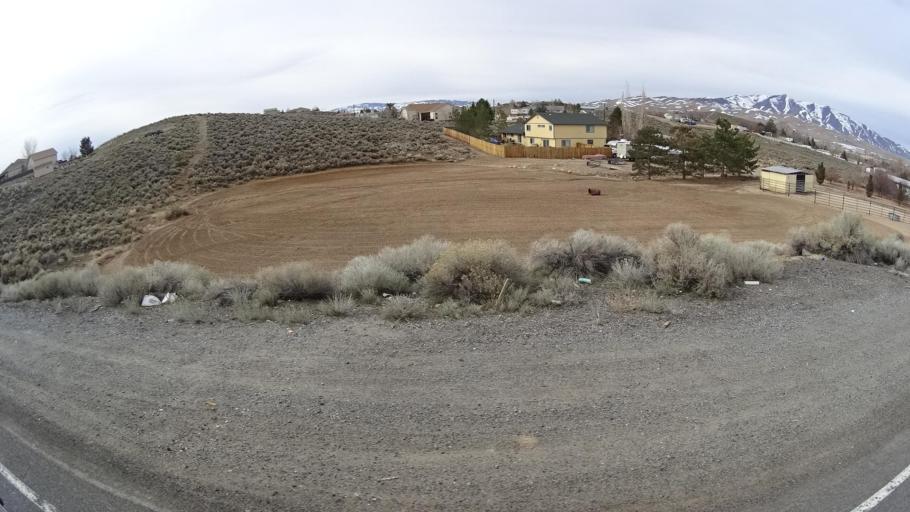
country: US
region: Nevada
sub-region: Washoe County
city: Golden Valley
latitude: 39.6067
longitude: -119.8113
